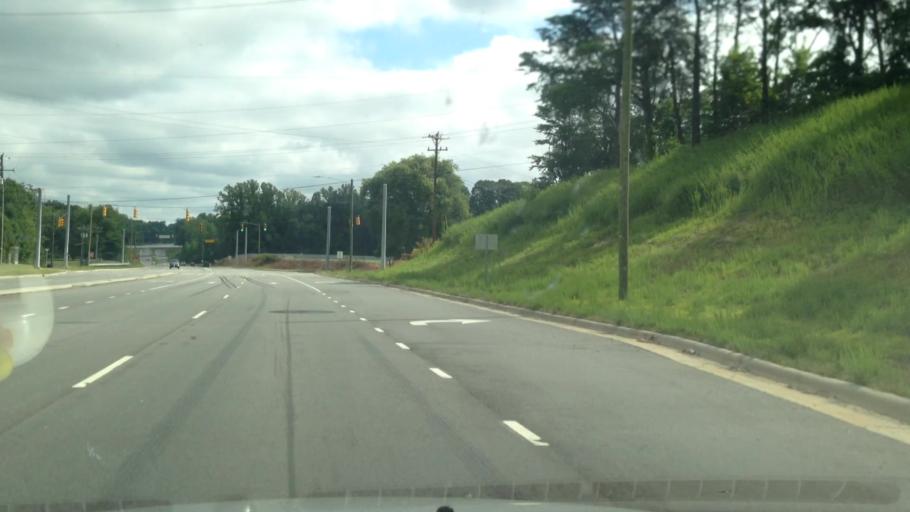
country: US
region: North Carolina
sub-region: Rockingham County
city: Reidsville
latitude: 36.3642
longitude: -79.6823
